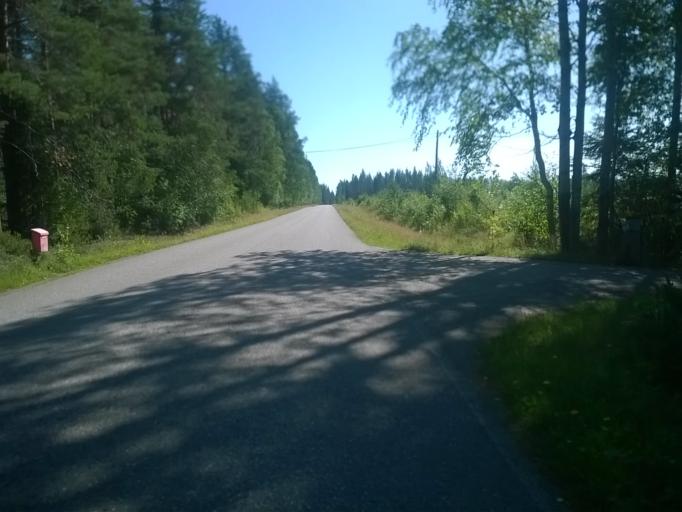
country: FI
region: Kainuu
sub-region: Kehys-Kainuu
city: Kuhmo
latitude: 64.1355
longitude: 29.4276
